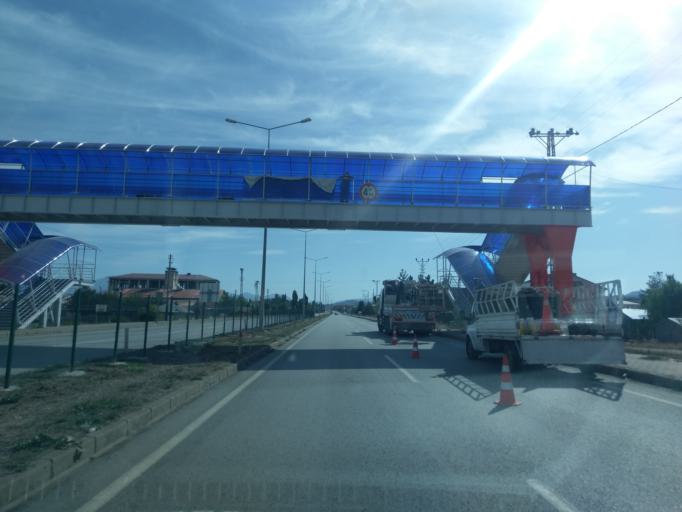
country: TR
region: Sivas
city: Imranli
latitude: 39.8713
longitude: 38.1135
